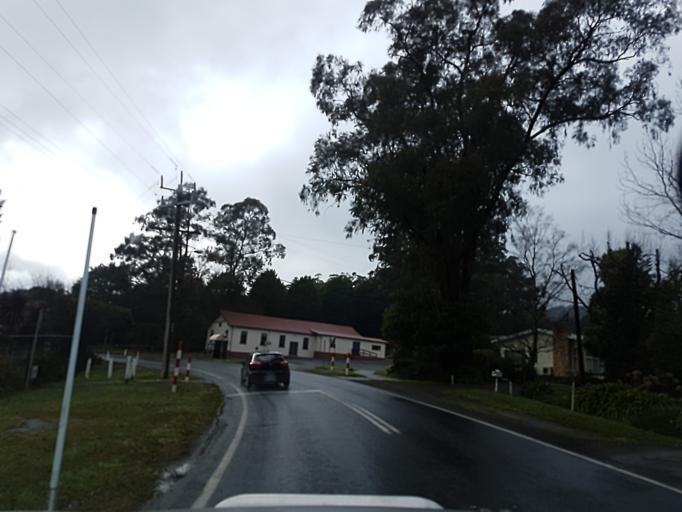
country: AU
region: Victoria
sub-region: Yarra Ranges
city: Millgrove
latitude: -37.7427
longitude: 145.7355
